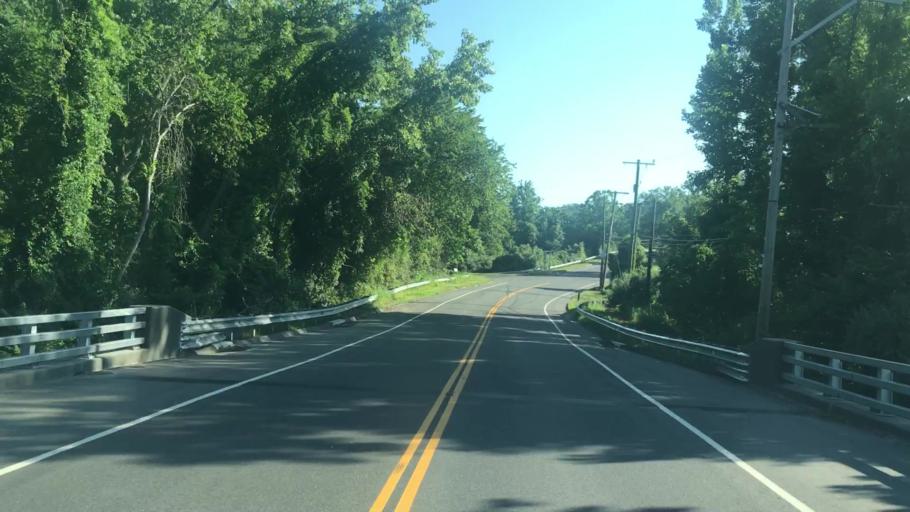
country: US
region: Connecticut
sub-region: New Haven County
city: Heritage Village
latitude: 41.4397
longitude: -73.2514
